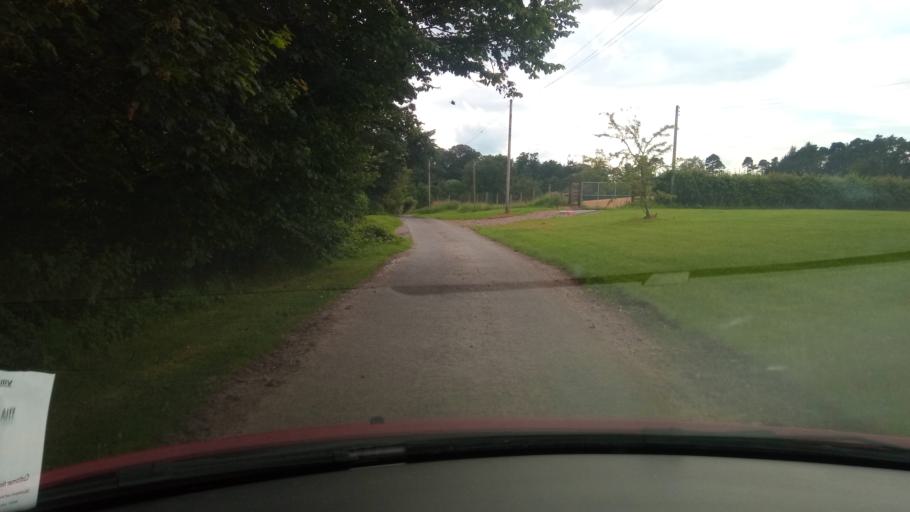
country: GB
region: Scotland
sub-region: The Scottish Borders
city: Jedburgh
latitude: 55.4310
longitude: -2.6353
